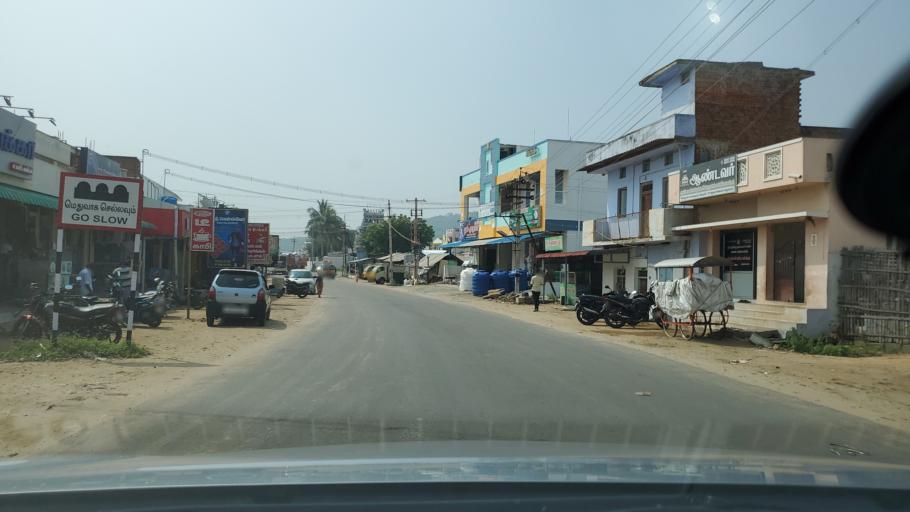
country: IN
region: Tamil Nadu
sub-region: Erode
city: Chennimalai
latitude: 11.1673
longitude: 77.6024
